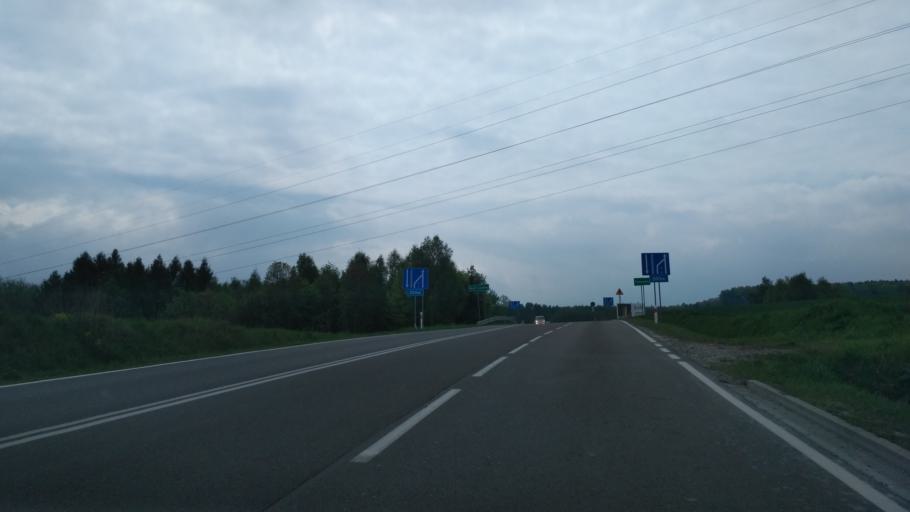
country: PL
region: Lesser Poland Voivodeship
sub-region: Powiat tarnowski
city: Tarnowiec
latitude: 49.9482
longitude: 21.0145
